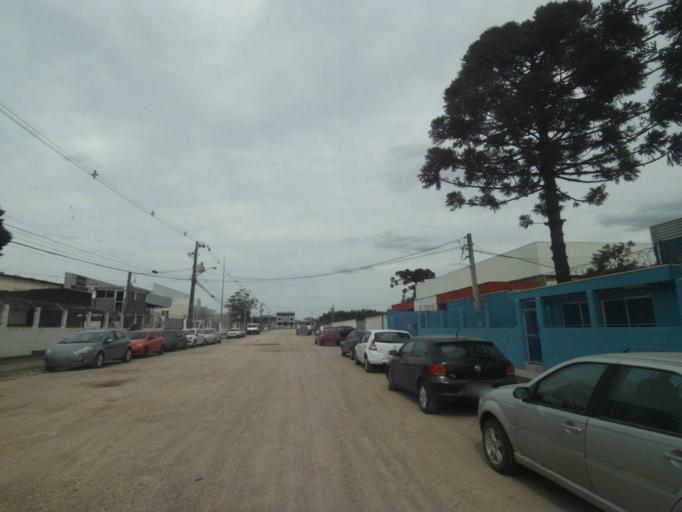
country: BR
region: Parana
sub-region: Araucaria
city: Araucaria
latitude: -25.5186
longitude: -49.3327
